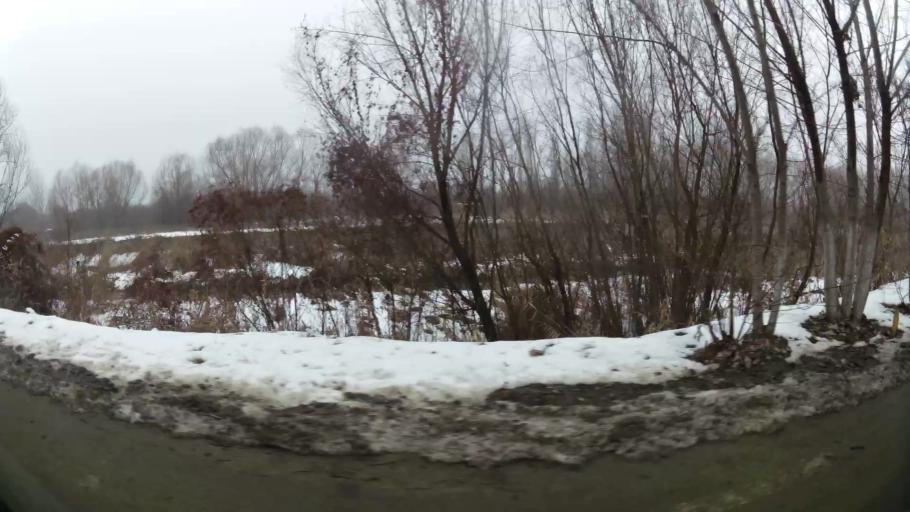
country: RO
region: Ilfov
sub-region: Comuna Chiajna
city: Chiajna
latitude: 44.4649
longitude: 25.9777
